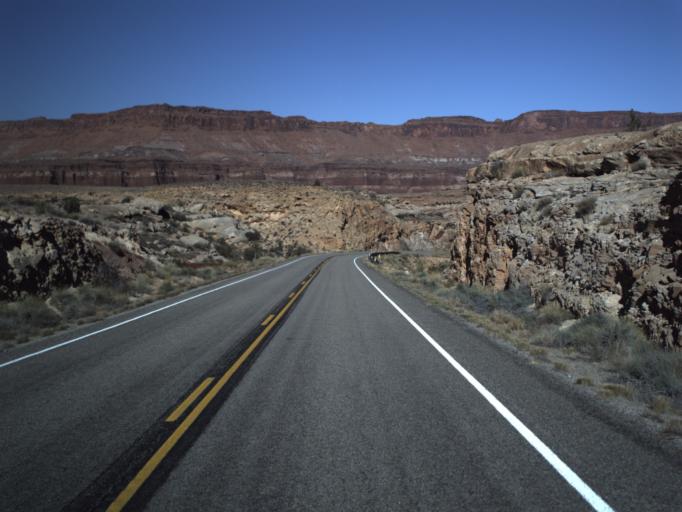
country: US
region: Utah
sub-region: San Juan County
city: Blanding
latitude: 37.8850
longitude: -110.3634
